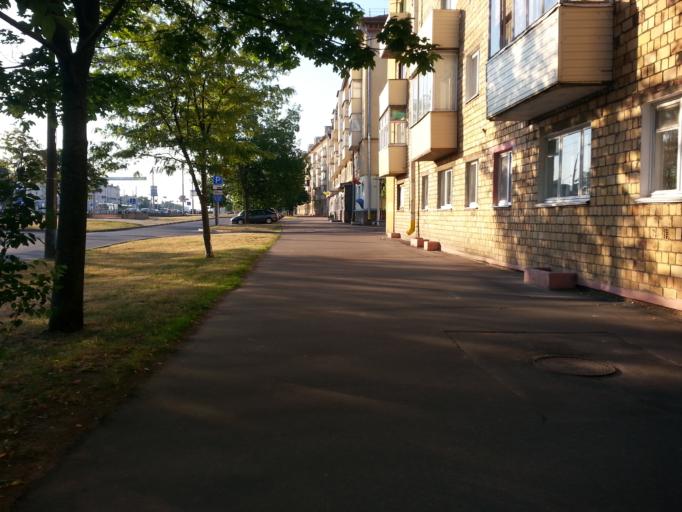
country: BY
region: Minsk
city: Vyaliki Trastsyanets
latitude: 53.8704
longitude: 27.6433
